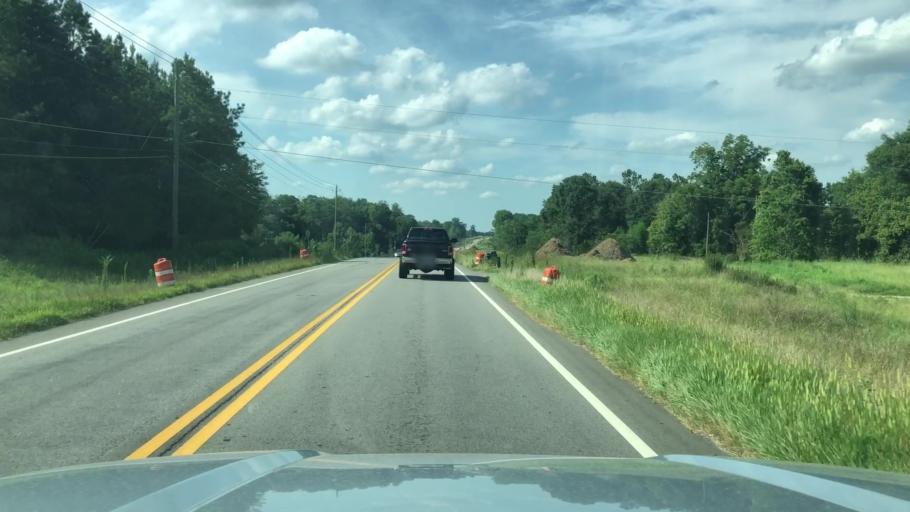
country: US
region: Georgia
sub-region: Paulding County
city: Hiram
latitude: 33.8257
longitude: -84.7591
